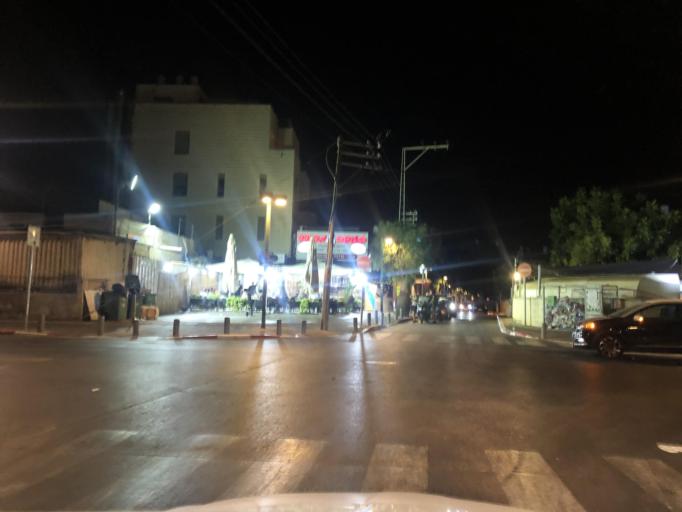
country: IL
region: Tel Aviv
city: Azor
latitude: 32.0467
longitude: 34.7919
